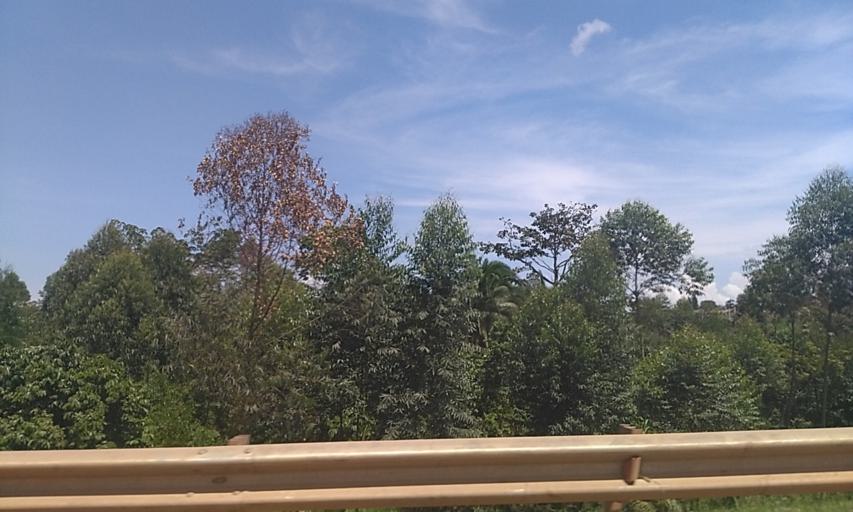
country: UG
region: Central Region
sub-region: Wakiso District
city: Wakiso
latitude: 0.4066
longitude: 32.4698
